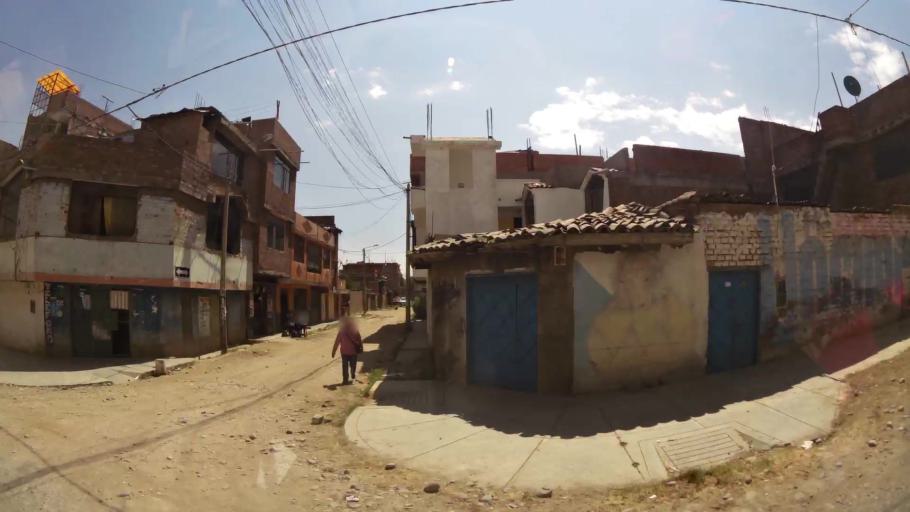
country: PE
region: Junin
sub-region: Provincia de Huancayo
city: El Tambo
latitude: -12.0671
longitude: -75.2238
